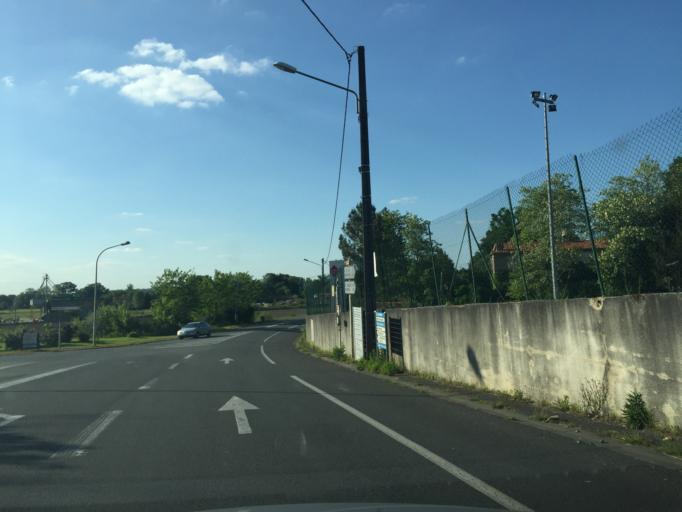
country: FR
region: Aquitaine
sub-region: Departement de la Dordogne
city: La Roche-Chalais
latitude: 45.1565
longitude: 0.0073
